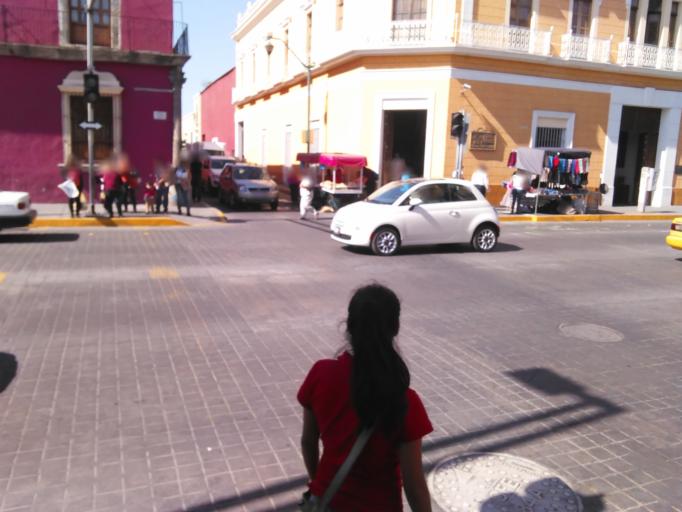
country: MX
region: Nayarit
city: Tepic
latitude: 21.5101
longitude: -104.8922
